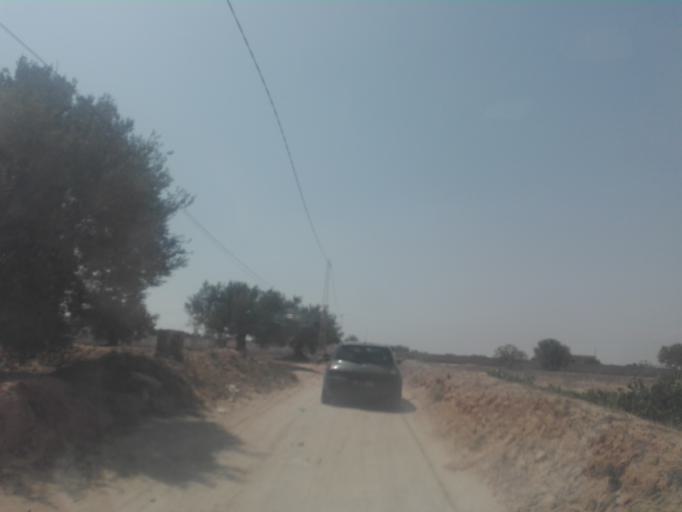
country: TN
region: Madanin
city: Zarzis
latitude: 33.5264
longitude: 11.0660
